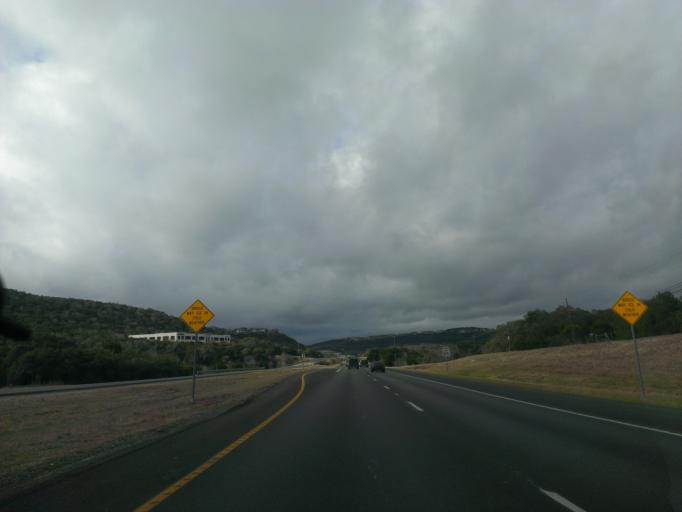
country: US
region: Texas
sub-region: Williamson County
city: Jollyville
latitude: 30.3802
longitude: -97.7757
